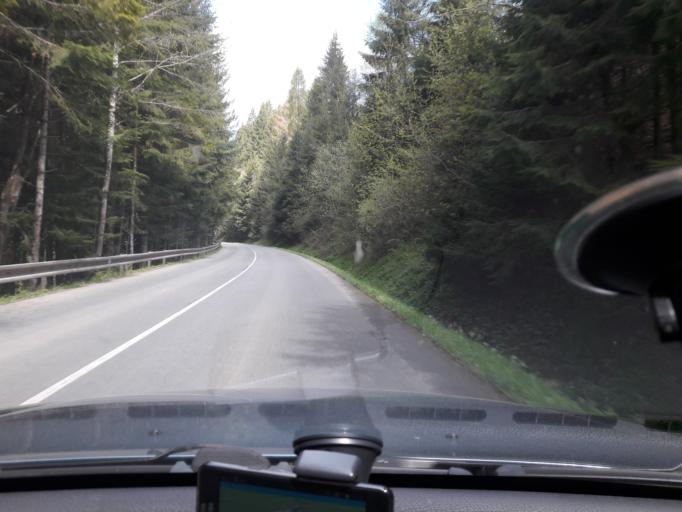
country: SK
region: Banskobystricky
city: Hrinova
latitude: 48.6059
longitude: 19.5590
